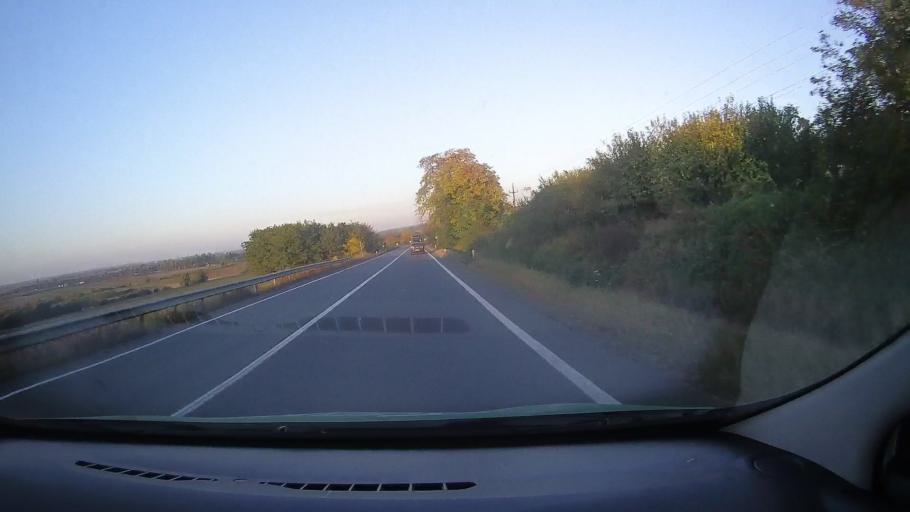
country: RO
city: Dioszeg
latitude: 47.2761
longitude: 21.9803
